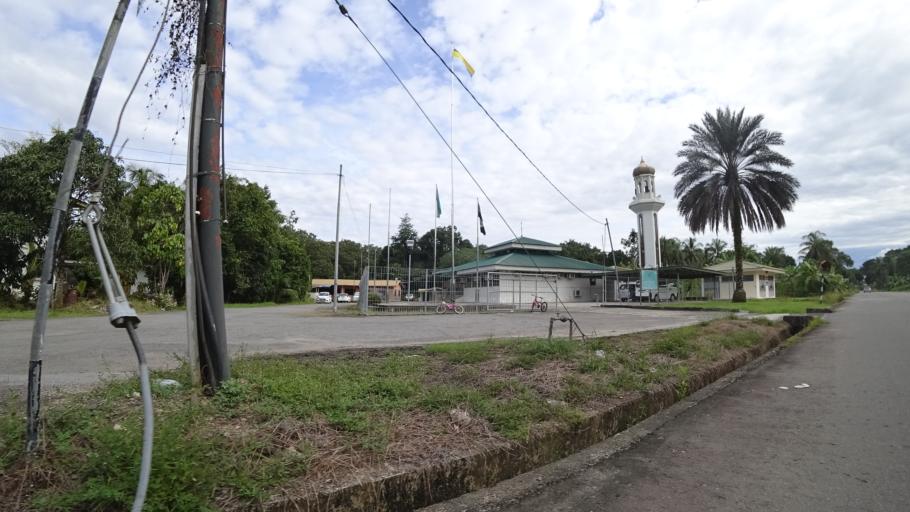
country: MY
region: Sarawak
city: Limbang
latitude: 4.8237
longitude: 114.9476
